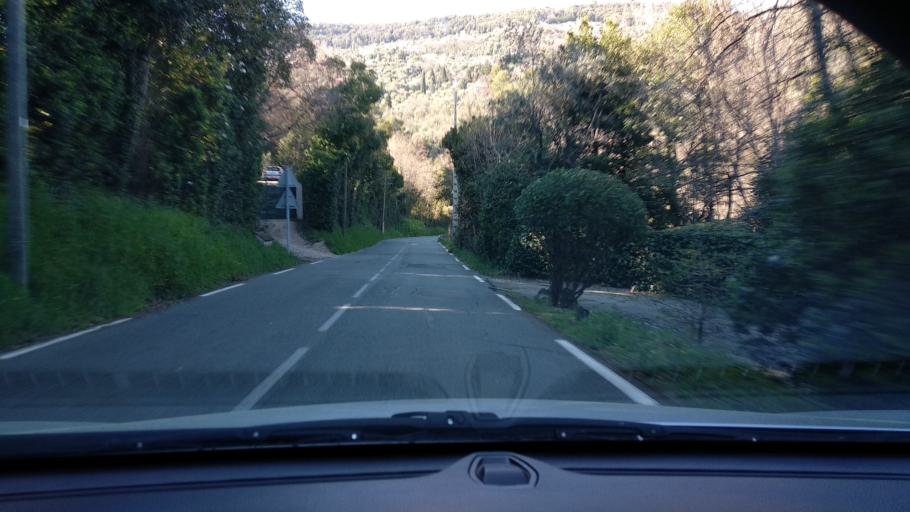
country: FR
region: Provence-Alpes-Cote d'Azur
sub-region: Departement des Alpes-Maritimes
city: Grasse
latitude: 43.6588
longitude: 6.9031
